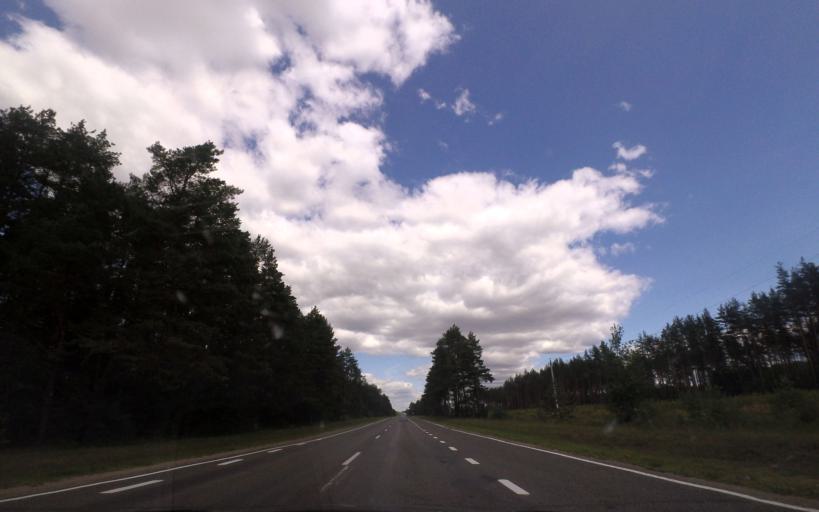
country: BY
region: Grodnenskaya
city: Hrodna
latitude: 53.7967
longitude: 23.8565
